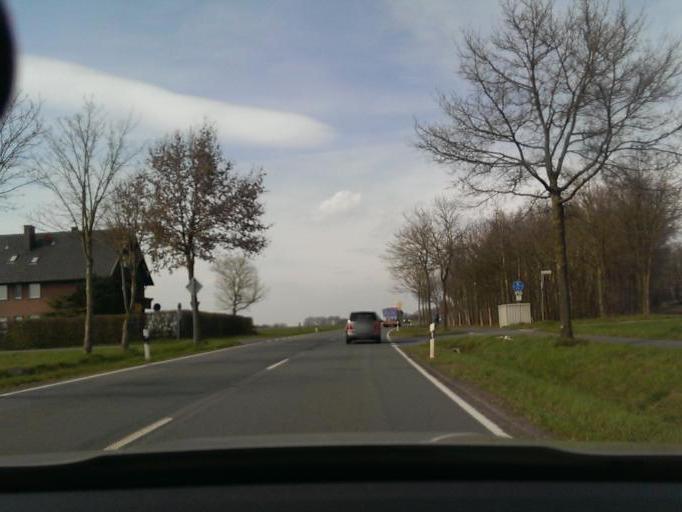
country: DE
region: North Rhine-Westphalia
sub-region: Regierungsbezirk Detmold
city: Hovelhof
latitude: 51.8015
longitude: 8.6169
